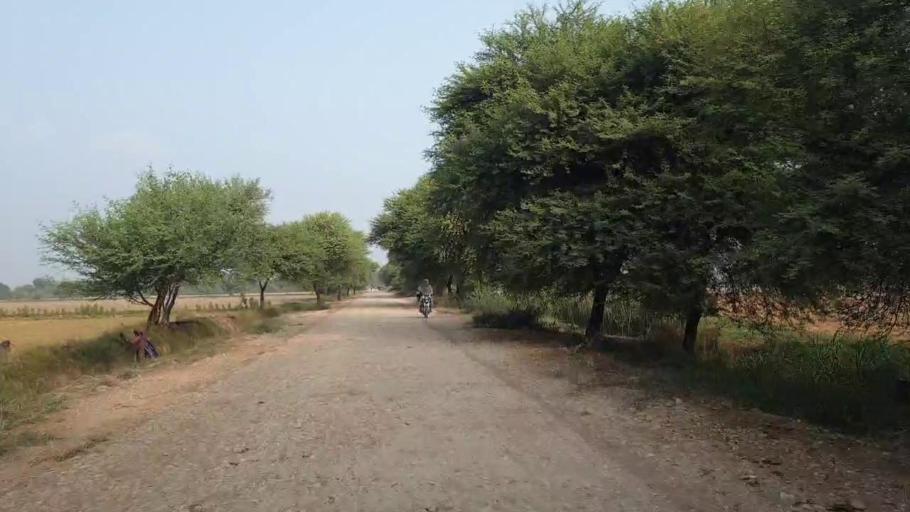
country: PK
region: Sindh
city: Tando Muhammad Khan
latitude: 25.1369
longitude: 68.5934
